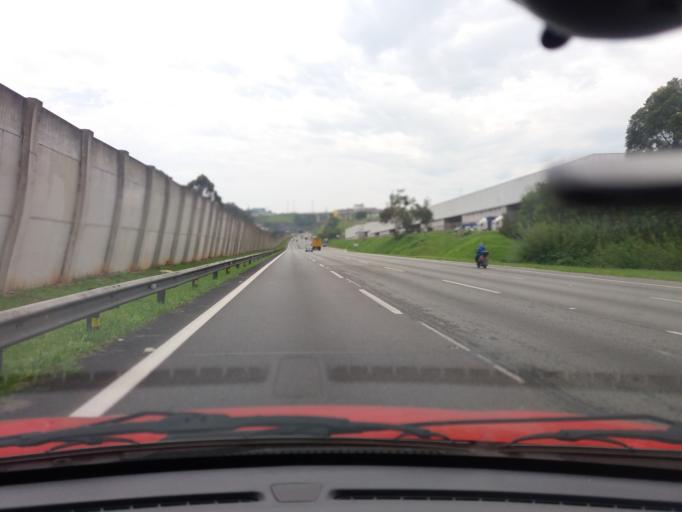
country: BR
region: Sao Paulo
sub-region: Carapicuiba
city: Carapicuiba
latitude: -23.4975
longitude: -46.8172
